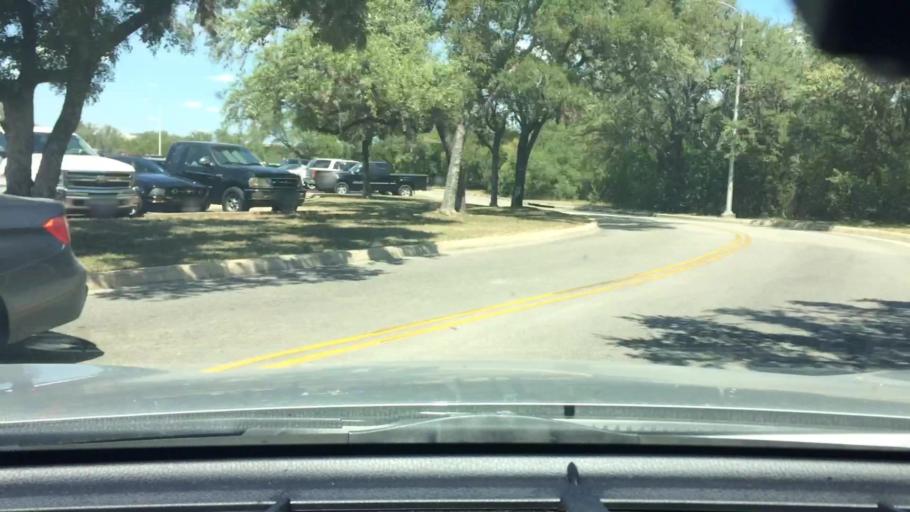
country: US
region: Texas
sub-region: Bexar County
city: Shavano Park
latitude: 29.5805
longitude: -98.6144
